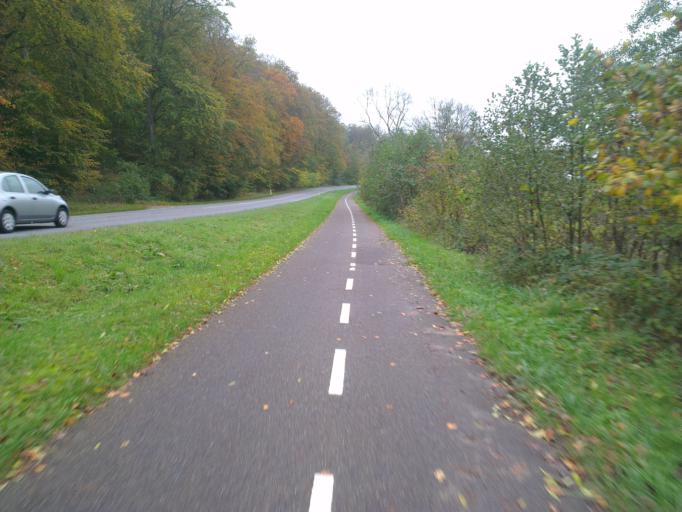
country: DK
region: Capital Region
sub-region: Frederikssund Kommune
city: Frederikssund
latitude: 55.8528
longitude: 12.0213
